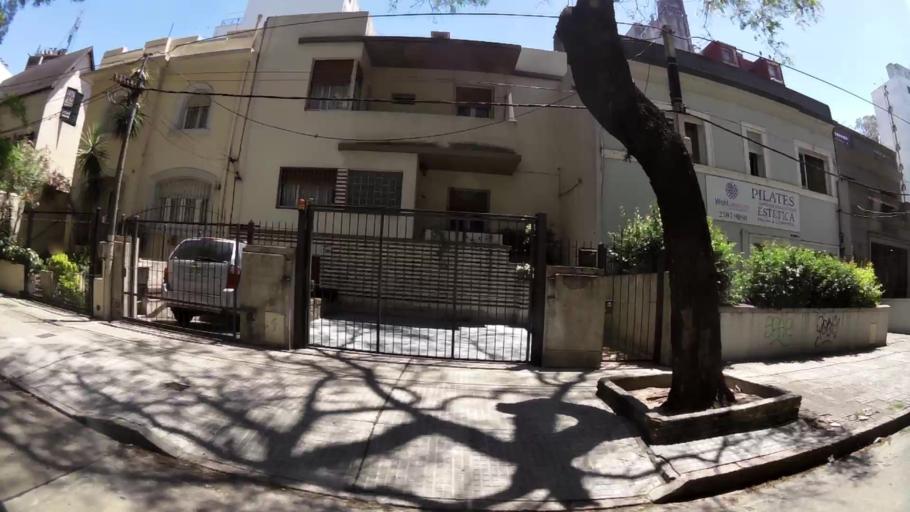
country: UY
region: Montevideo
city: Montevideo
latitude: -34.9120
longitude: -56.1524
